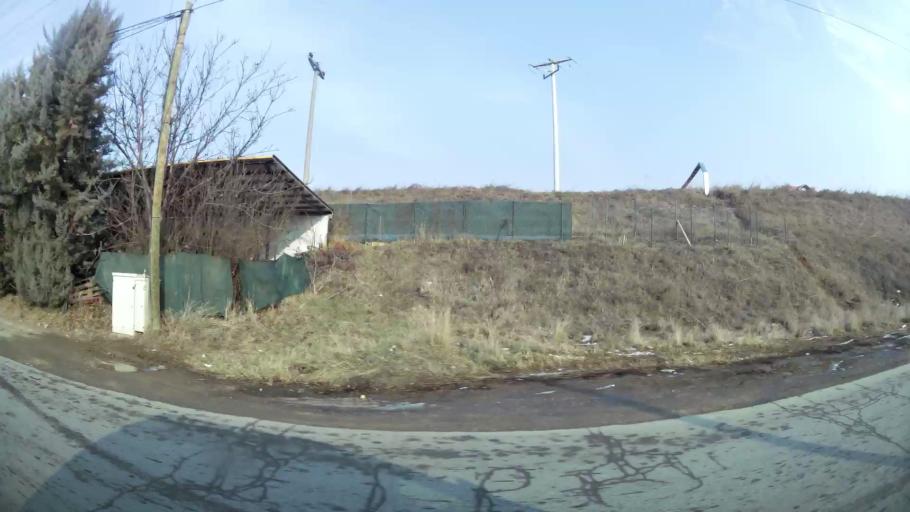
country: MK
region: Ilinden
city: Marino
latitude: 41.9860
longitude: 21.5940
